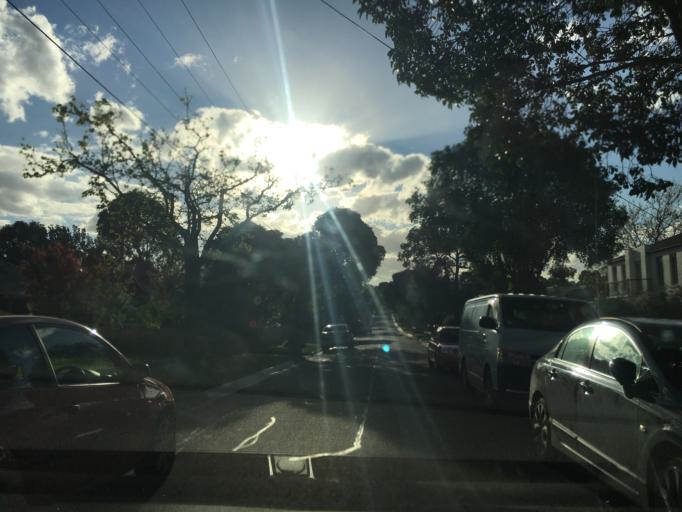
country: AU
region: Victoria
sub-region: Whitehorse
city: Vermont South
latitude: -37.8780
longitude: 145.1769
